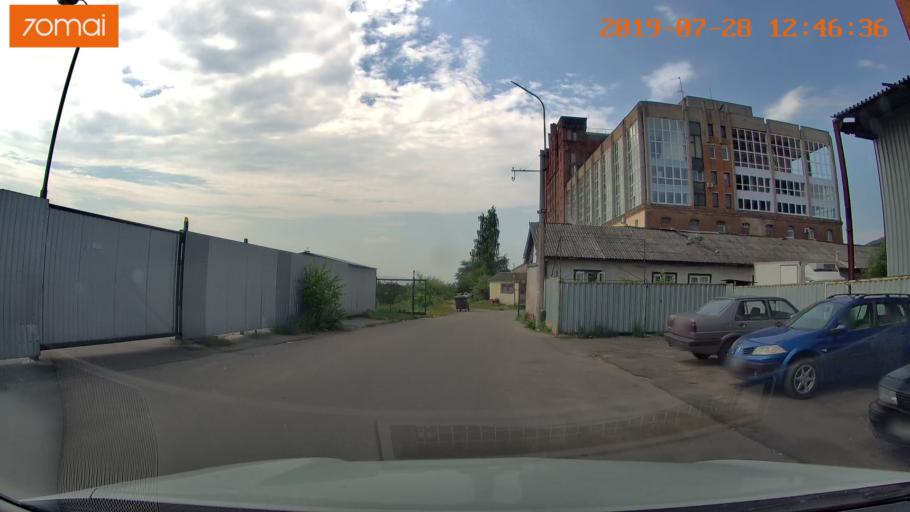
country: RU
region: Kaliningrad
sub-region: Gorod Kaliningrad
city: Kaliningrad
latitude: 54.7056
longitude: 20.4554
